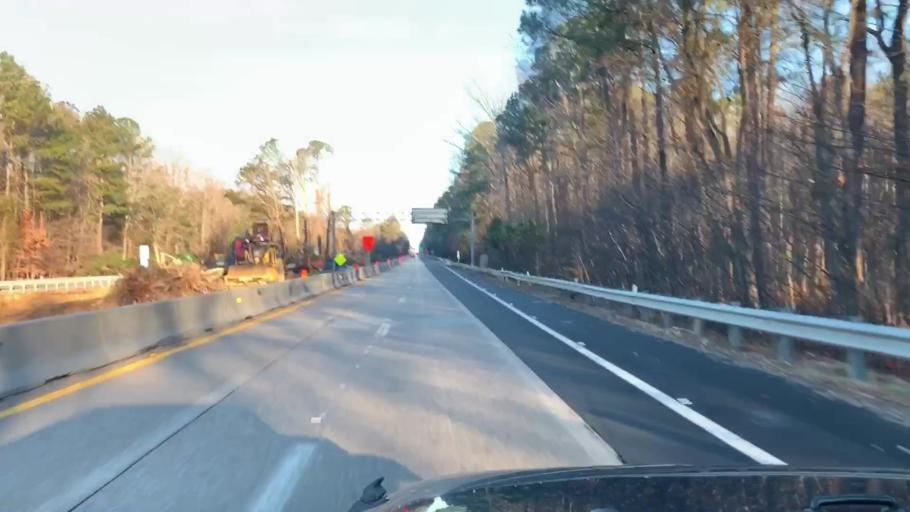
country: US
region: Virginia
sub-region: City of Williamsburg
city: Williamsburg
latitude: 37.2951
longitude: -76.6769
